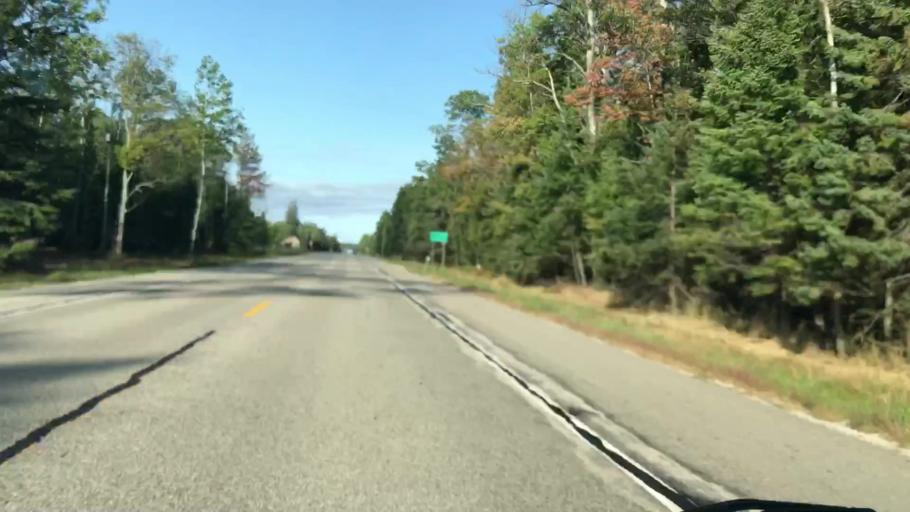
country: US
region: Michigan
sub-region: Luce County
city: Newberry
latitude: 46.3034
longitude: -85.3596
